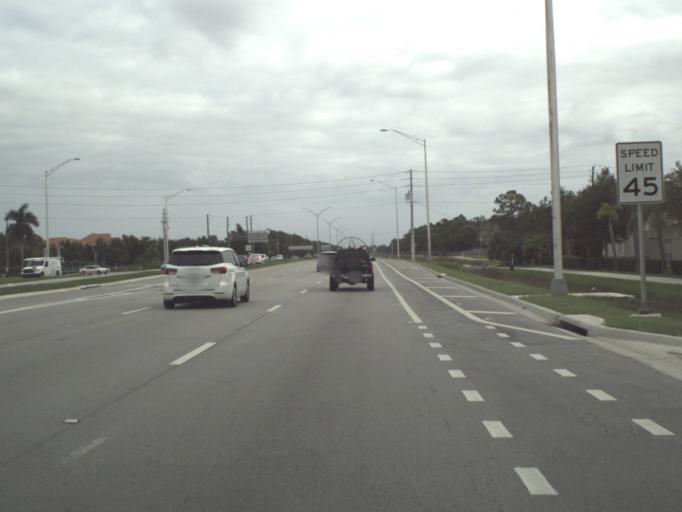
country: US
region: Florida
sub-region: Collier County
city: Lely Resort
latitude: 26.0655
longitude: -81.6974
